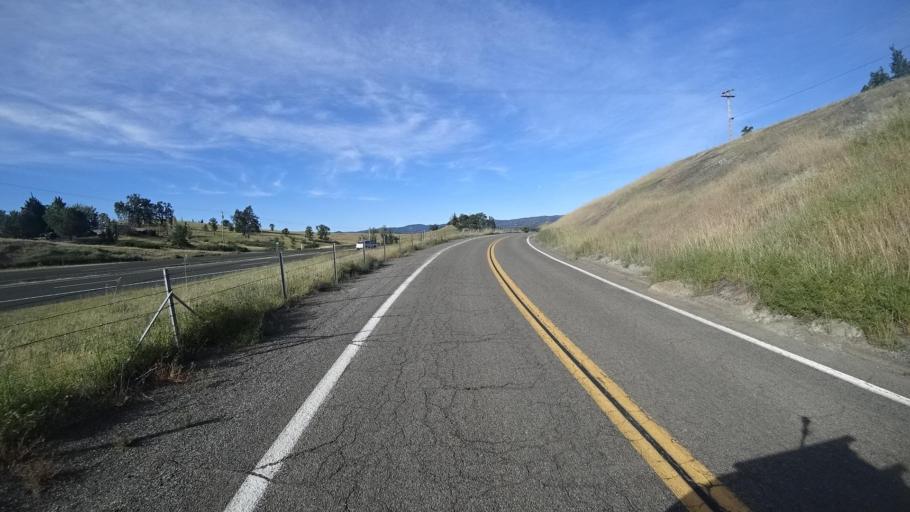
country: US
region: California
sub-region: Lake County
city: North Lakeport
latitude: 39.0899
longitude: -122.9182
